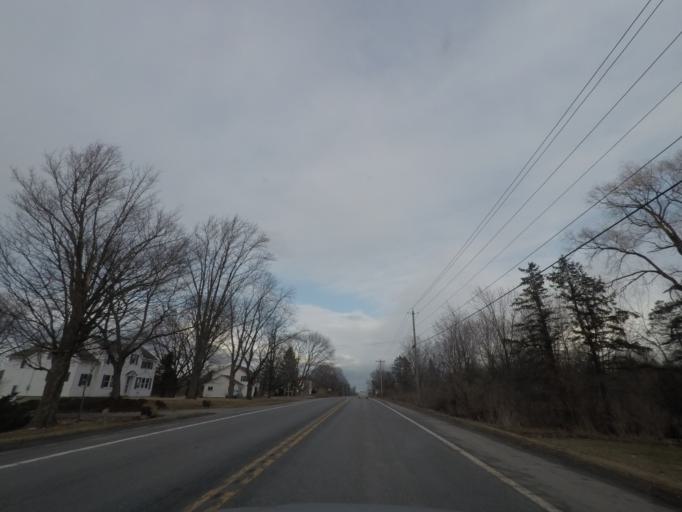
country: US
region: New York
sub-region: Oneida County
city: Vernon
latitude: 43.0740
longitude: -75.4690
